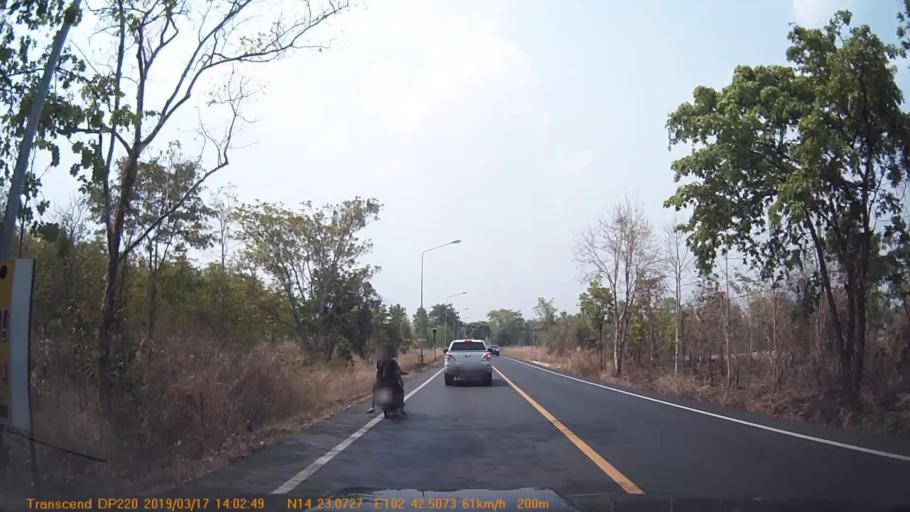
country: TH
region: Buriram
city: Pa Kham
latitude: 14.3848
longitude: 102.7083
